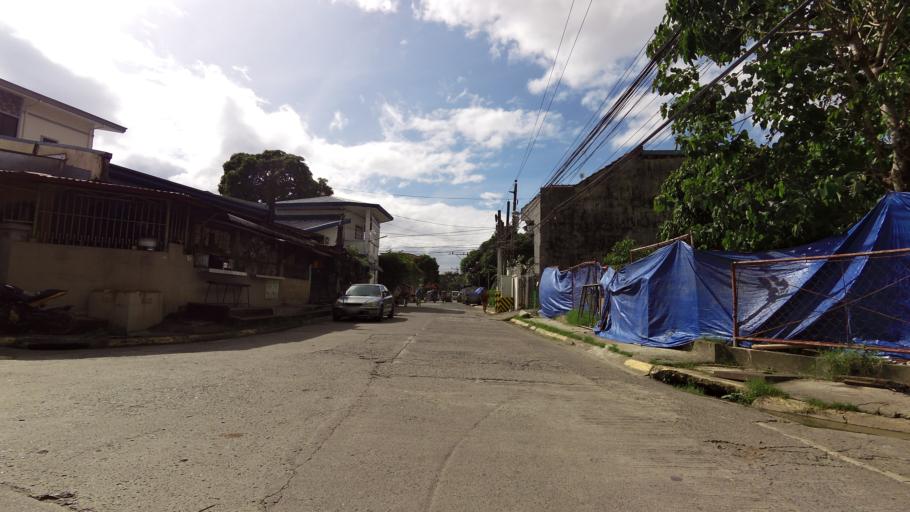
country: PH
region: Calabarzon
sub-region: Province of Rizal
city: Cainta
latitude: 14.5778
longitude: 121.1076
